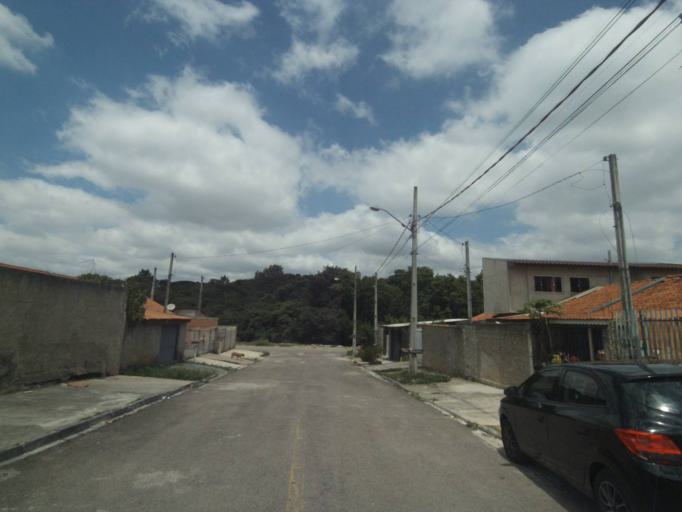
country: BR
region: Parana
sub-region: Curitiba
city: Curitiba
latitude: -25.5170
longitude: -49.3176
